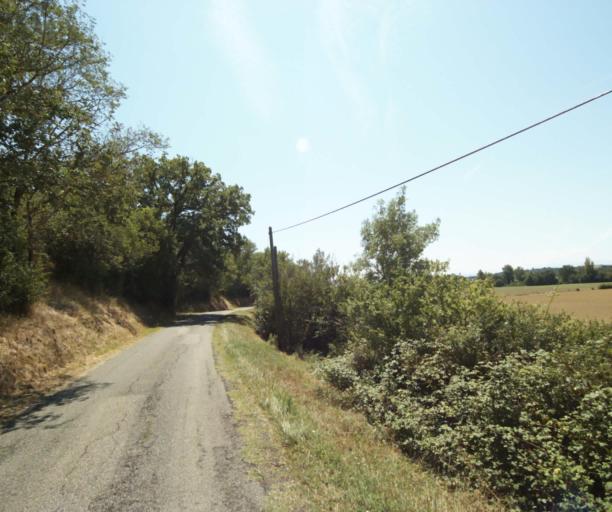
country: FR
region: Midi-Pyrenees
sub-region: Departement de l'Ariege
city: Lezat-sur-Leze
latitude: 43.3035
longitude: 1.3457
